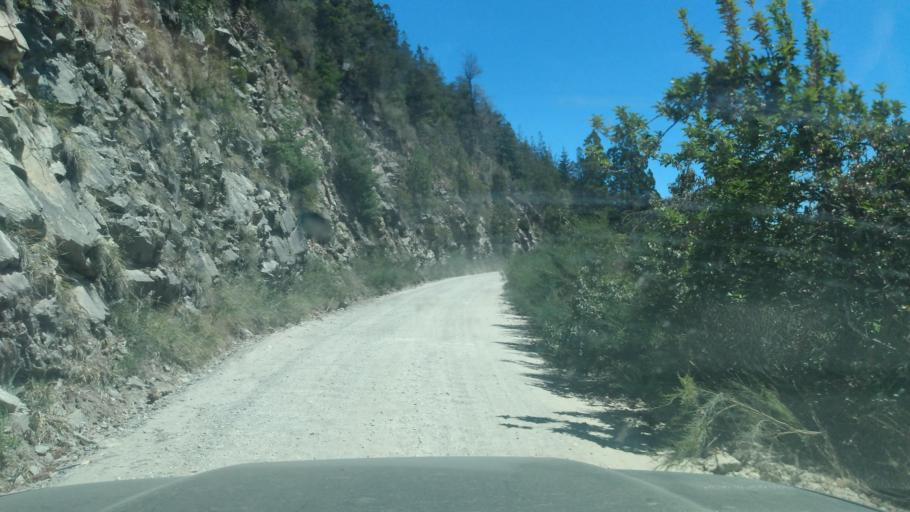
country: AR
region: Rio Negro
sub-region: Departamento de Bariloche
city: San Carlos de Bariloche
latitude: -41.1042
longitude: -71.4862
